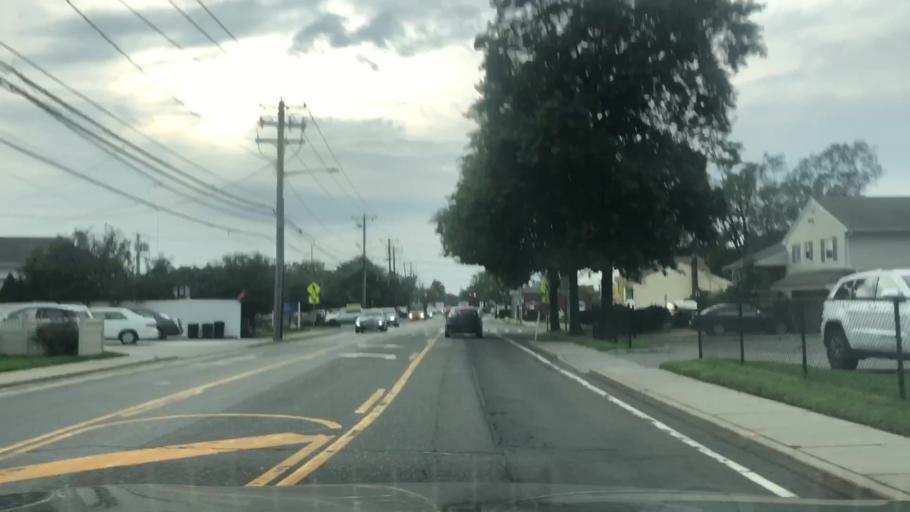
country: US
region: New York
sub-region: Nassau County
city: North Bellmore
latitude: 40.6913
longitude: -73.5399
